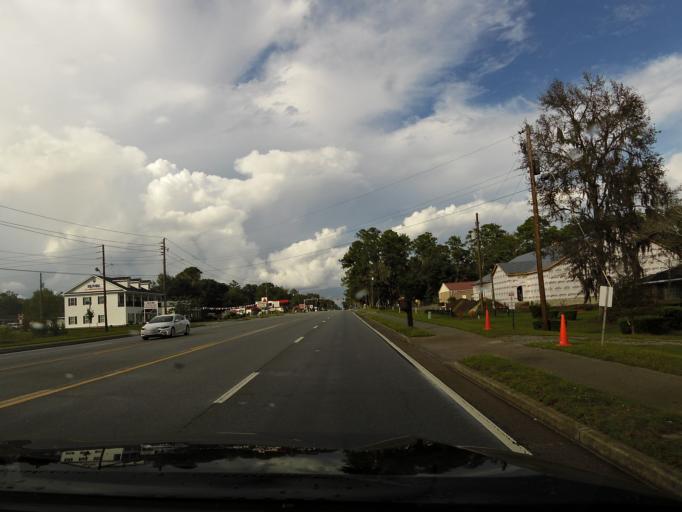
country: US
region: Georgia
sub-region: Liberty County
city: Walthourville
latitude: 31.7935
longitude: -81.6068
